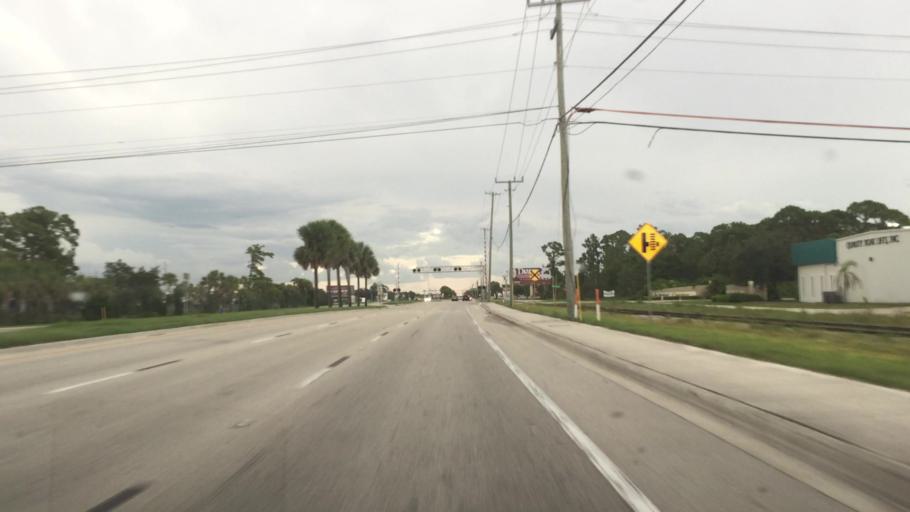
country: US
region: Florida
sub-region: Lee County
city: San Carlos Park
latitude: 26.4926
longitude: -81.8324
